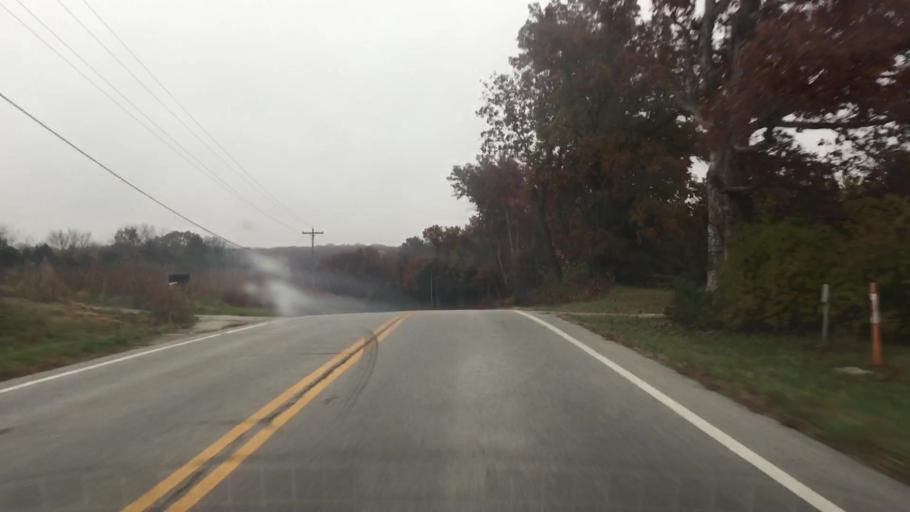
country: US
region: Missouri
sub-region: Callaway County
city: Fulton
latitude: 38.8842
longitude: -92.0942
